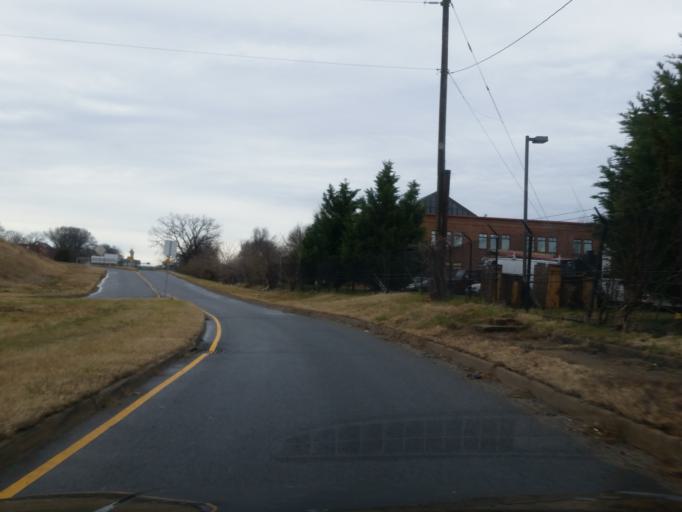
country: US
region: Virginia
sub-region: Arlington County
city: Arlington
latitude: 38.8746
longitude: -77.0825
